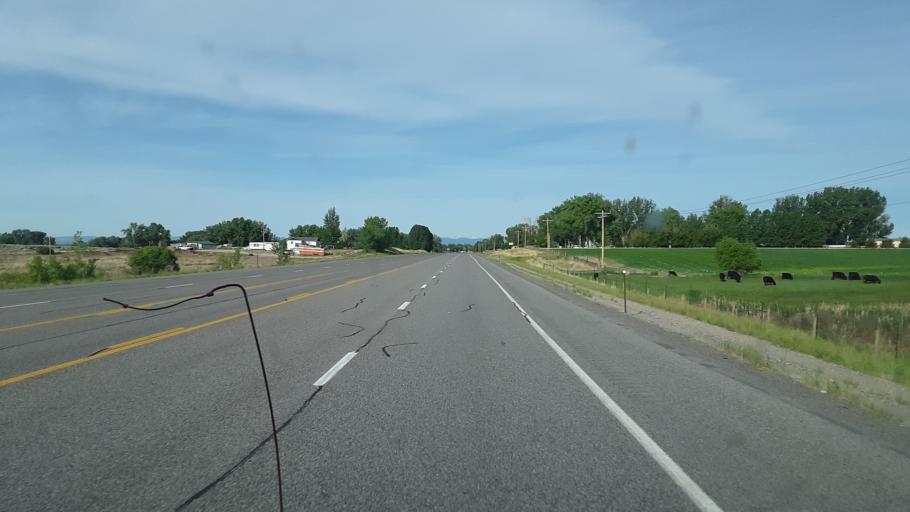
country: US
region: Wyoming
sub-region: Fremont County
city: Riverton
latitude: 43.1093
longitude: -108.3412
